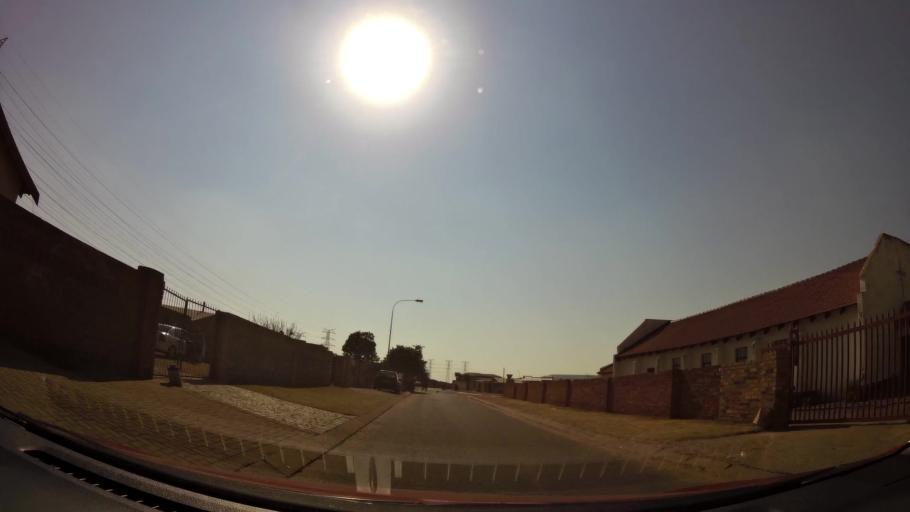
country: ZA
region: Gauteng
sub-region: City of Johannesburg Metropolitan Municipality
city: Soweto
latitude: -26.2414
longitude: 27.9375
